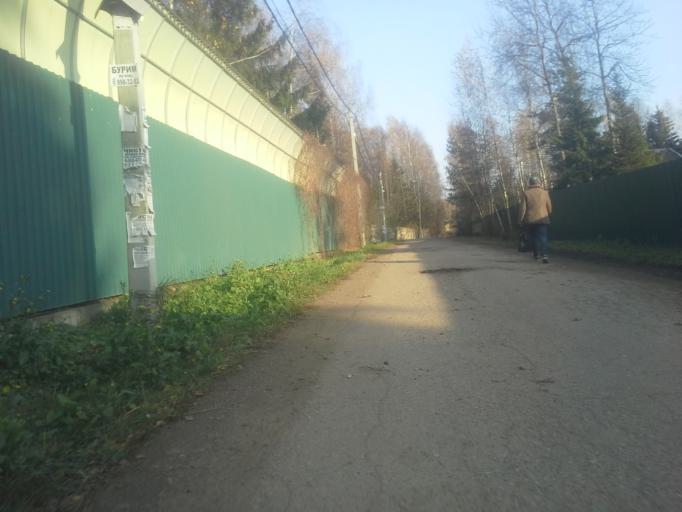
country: RU
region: Moskovskaya
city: Golitsyno
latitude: 55.5745
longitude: 37.0036
